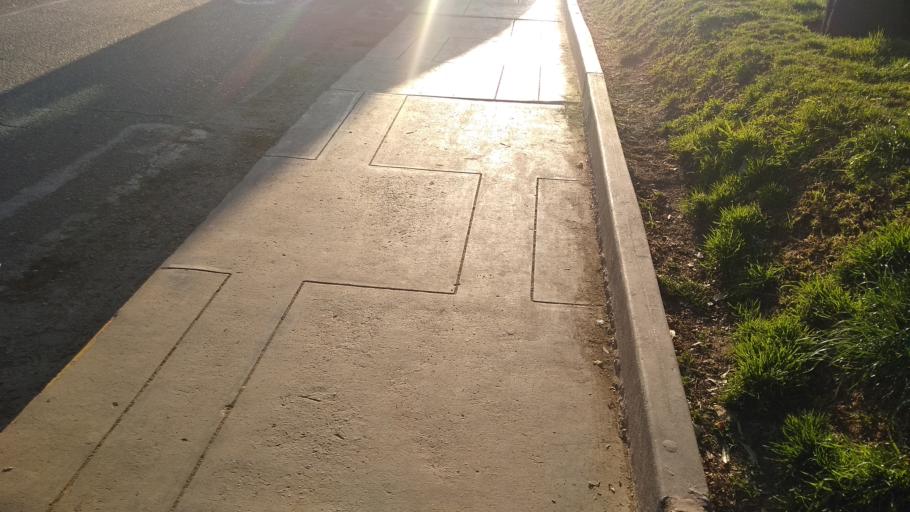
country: PE
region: Cusco
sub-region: Provincia de Cusco
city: Cusco
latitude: -13.5278
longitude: -71.9426
